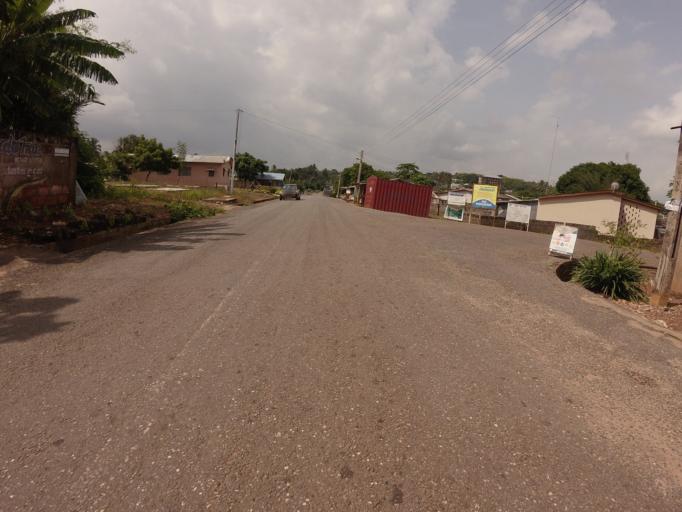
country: GH
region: Volta
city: Ho
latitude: 6.6160
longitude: 0.4759
